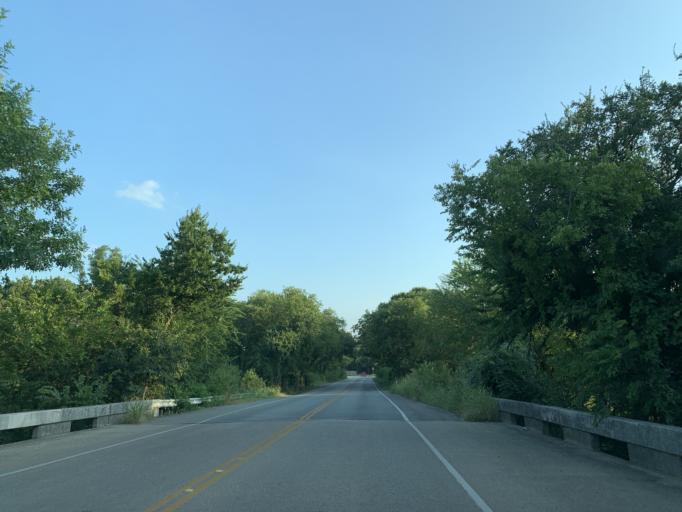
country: US
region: Texas
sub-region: Tarrant County
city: Hurst
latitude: 32.7818
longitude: -97.1785
